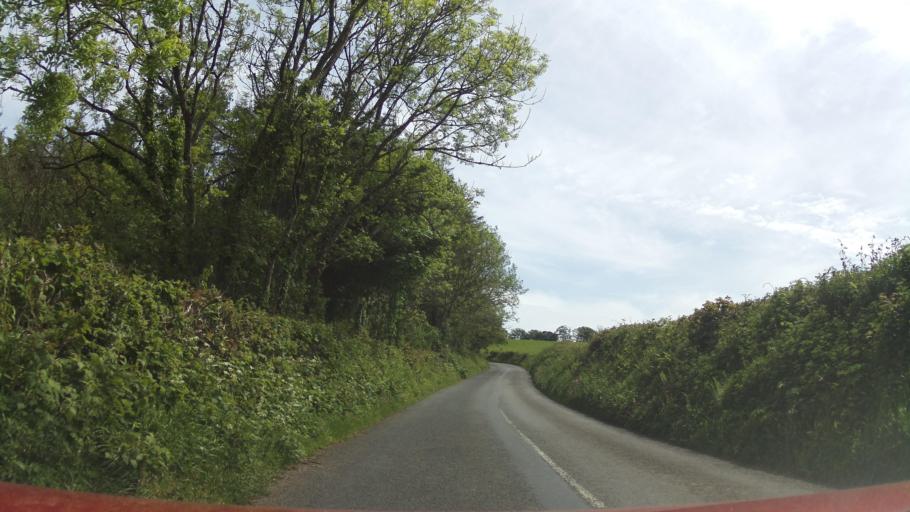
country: GB
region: England
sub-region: Devon
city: Kingsbridge
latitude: 50.3639
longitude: -3.7693
